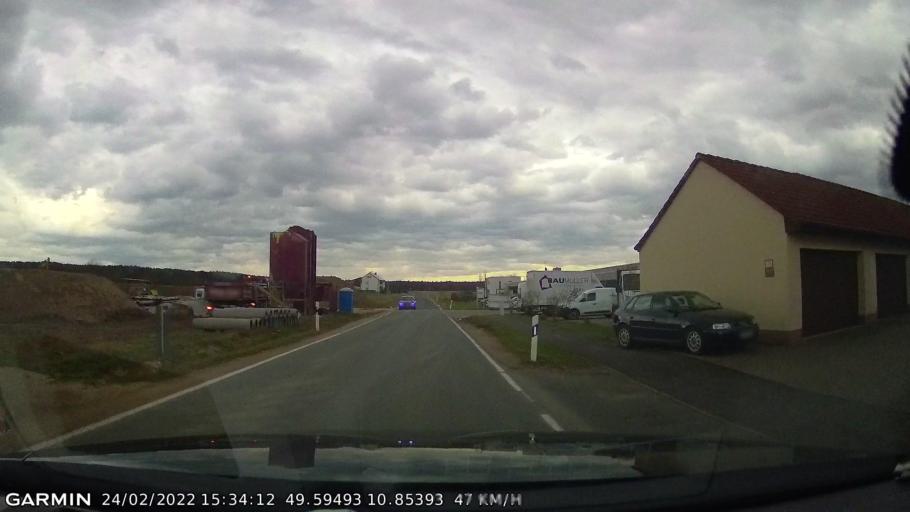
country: DE
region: Bavaria
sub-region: Regierungsbezirk Mittelfranken
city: Weisendorf
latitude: 49.5949
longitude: 10.8540
